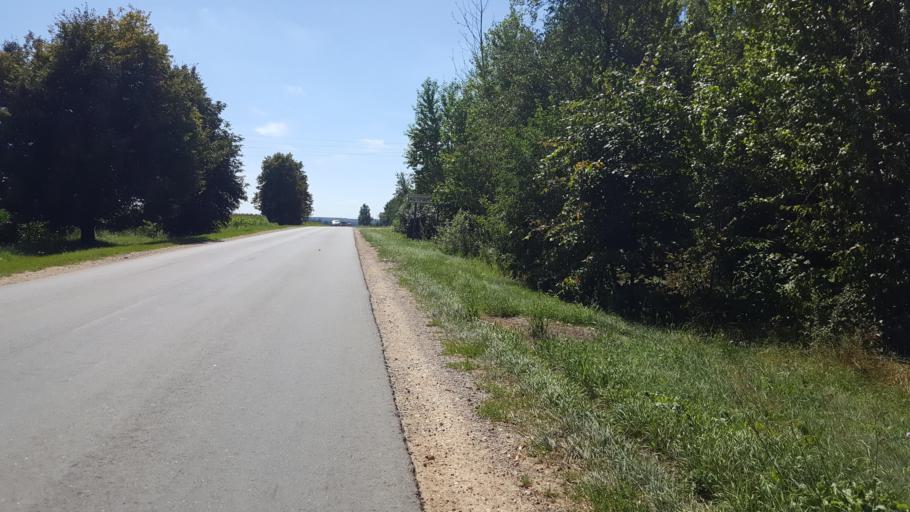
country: BY
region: Brest
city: Charnawchytsy
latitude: 52.2837
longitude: 23.6036
